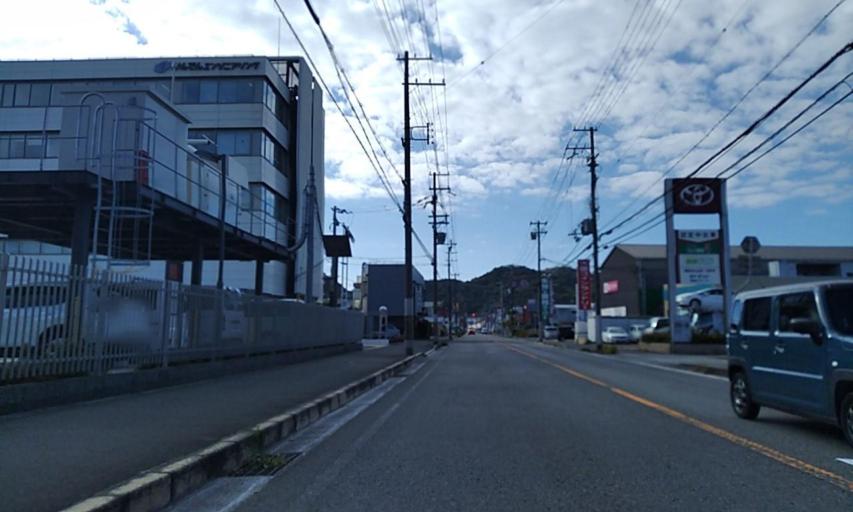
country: JP
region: Wakayama
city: Minato
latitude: 34.2001
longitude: 135.1590
